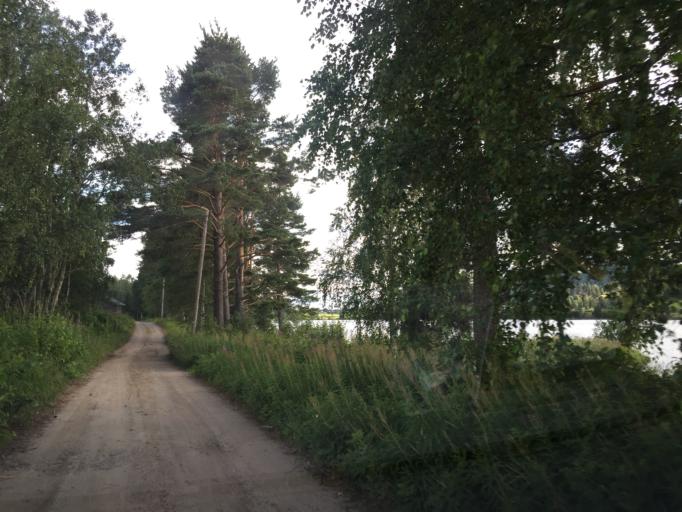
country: SE
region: Gaevleborg
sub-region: Ljusdals Kommun
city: Jaervsoe
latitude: 61.7478
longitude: 16.1720
